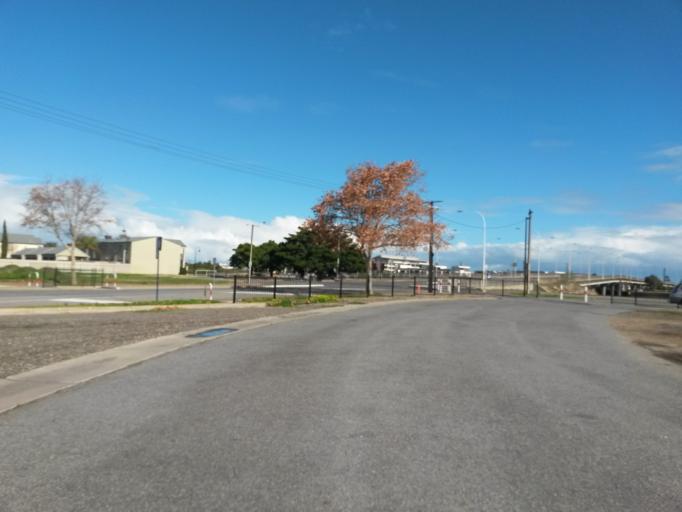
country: AU
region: South Australia
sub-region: Port Adelaide Enfield
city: Birkenhead
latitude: -34.8453
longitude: 138.4988
